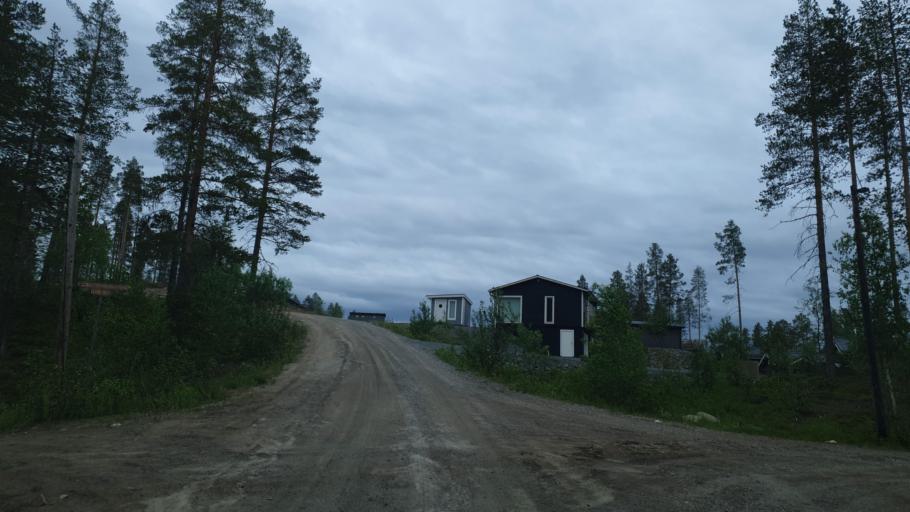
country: SE
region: Norrbotten
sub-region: Jokkmokks Kommun
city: Jokkmokk
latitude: 66.1535
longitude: 19.9917
